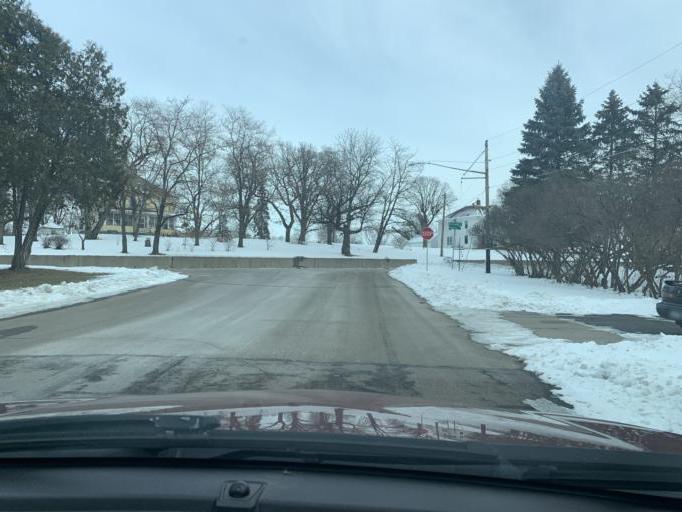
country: US
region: Minnesota
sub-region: Washington County
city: Saint Paul Park
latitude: 44.8460
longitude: -92.9876
